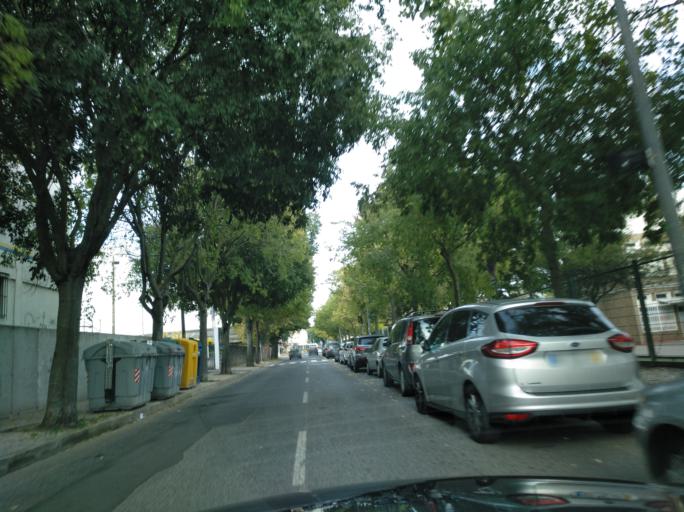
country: PT
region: Lisbon
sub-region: Sintra
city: Queluz
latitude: 38.7555
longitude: -9.2509
